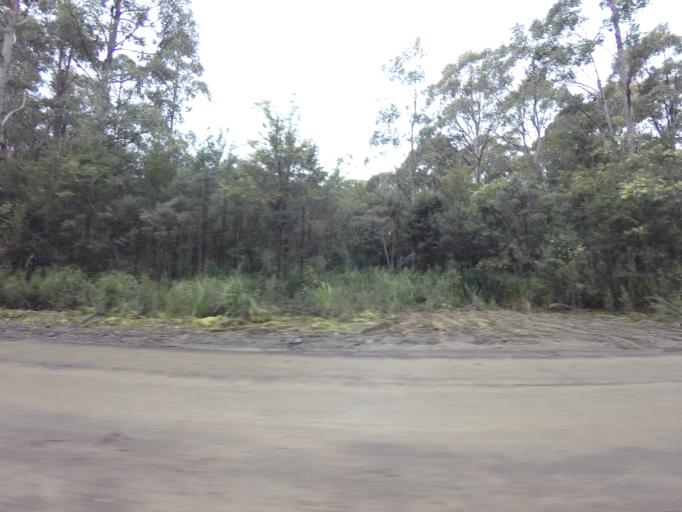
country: AU
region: Tasmania
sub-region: Huon Valley
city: Geeveston
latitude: -43.5187
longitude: 146.8839
